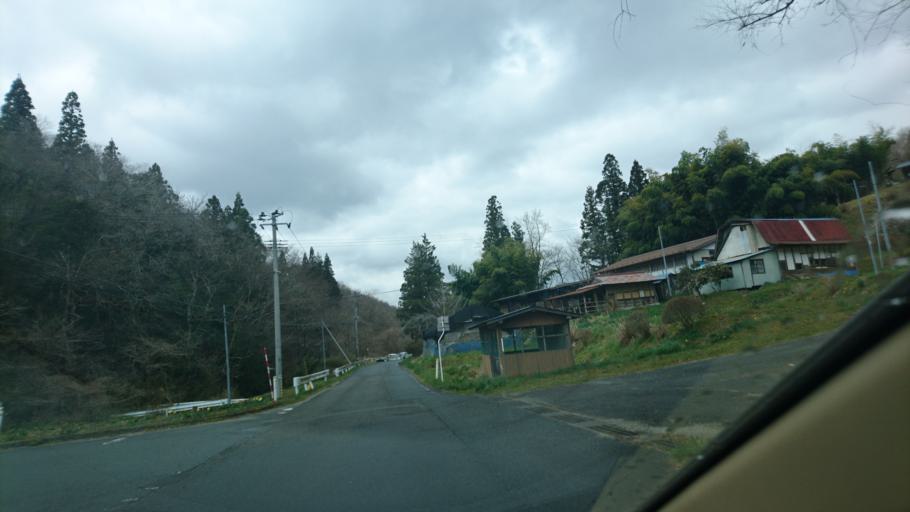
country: JP
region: Iwate
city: Ichinoseki
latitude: 38.9426
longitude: 141.3255
